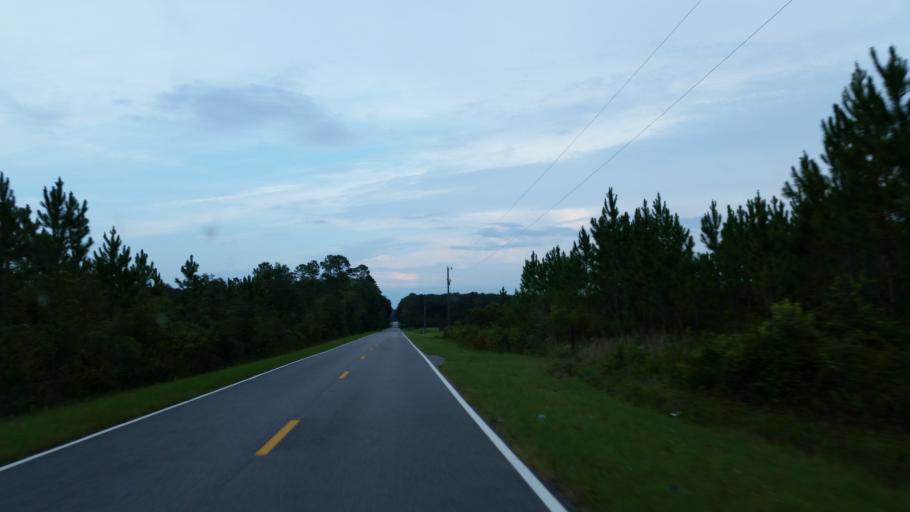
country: US
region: Georgia
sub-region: Lowndes County
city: Valdosta
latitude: 30.7458
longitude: -83.2436
